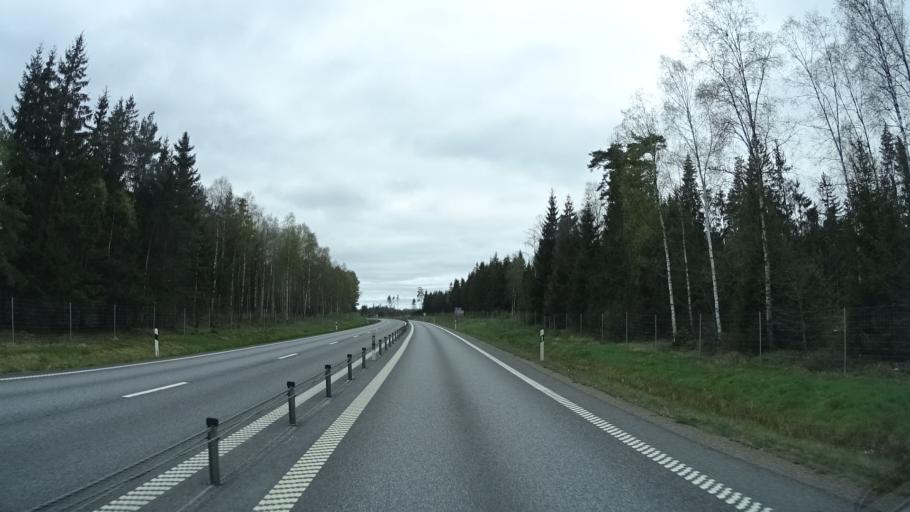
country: SE
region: Kronoberg
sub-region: Ljungby Kommun
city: Ljungby
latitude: 56.7996
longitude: 13.8605
